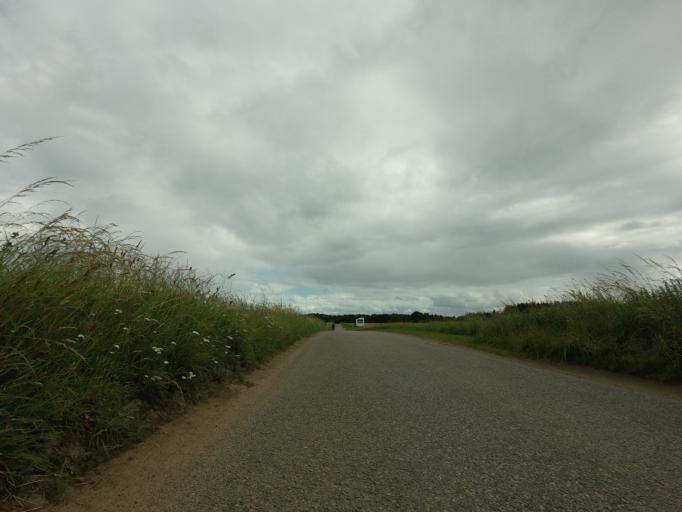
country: GB
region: Scotland
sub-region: Moray
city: Lhanbryd
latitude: 57.6618
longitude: -3.1852
